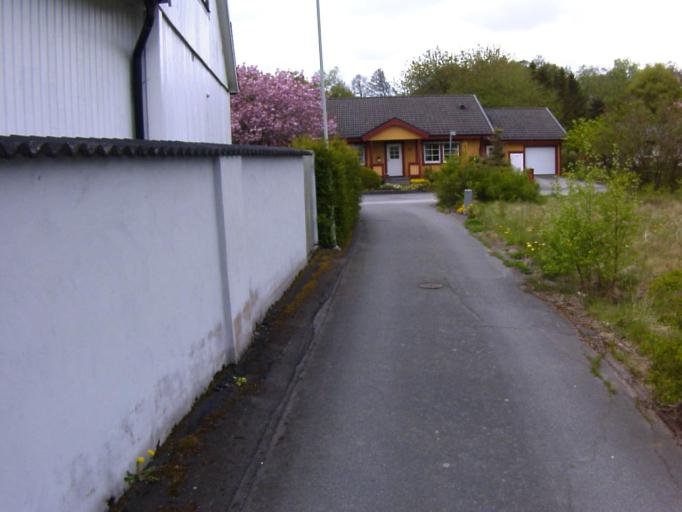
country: SE
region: Skane
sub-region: Kristianstads Kommun
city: Kristianstad
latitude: 56.0198
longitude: 14.1910
